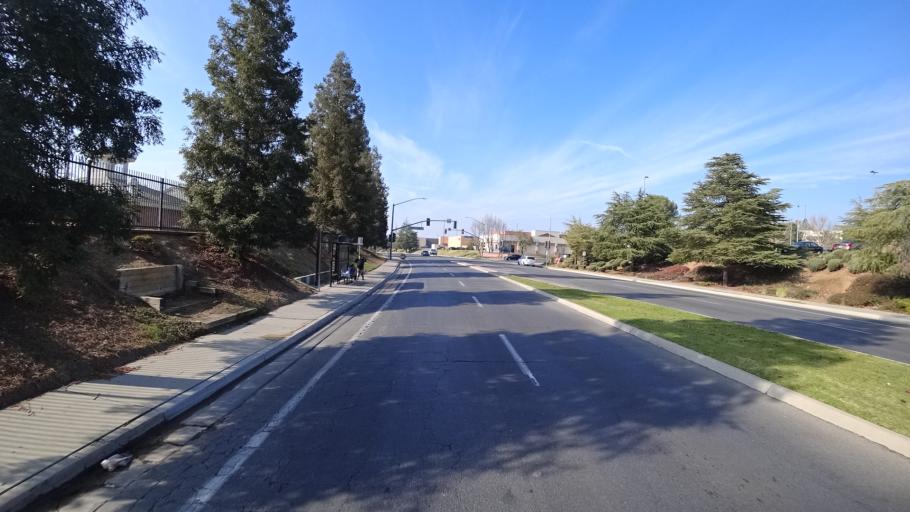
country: US
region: California
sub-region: Kern County
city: Bakersfield
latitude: 35.3921
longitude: -118.9568
